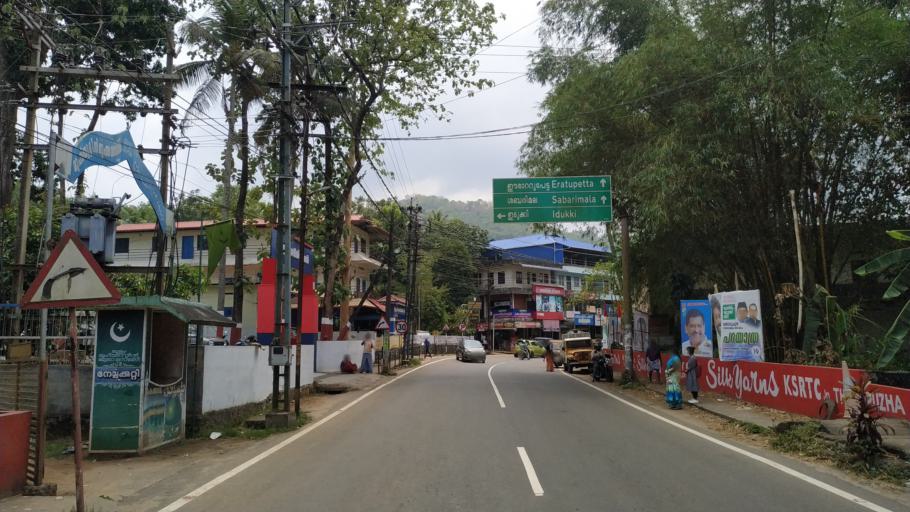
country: IN
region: Kerala
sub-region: Kottayam
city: Lalam
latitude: 9.8399
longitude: 76.7458
